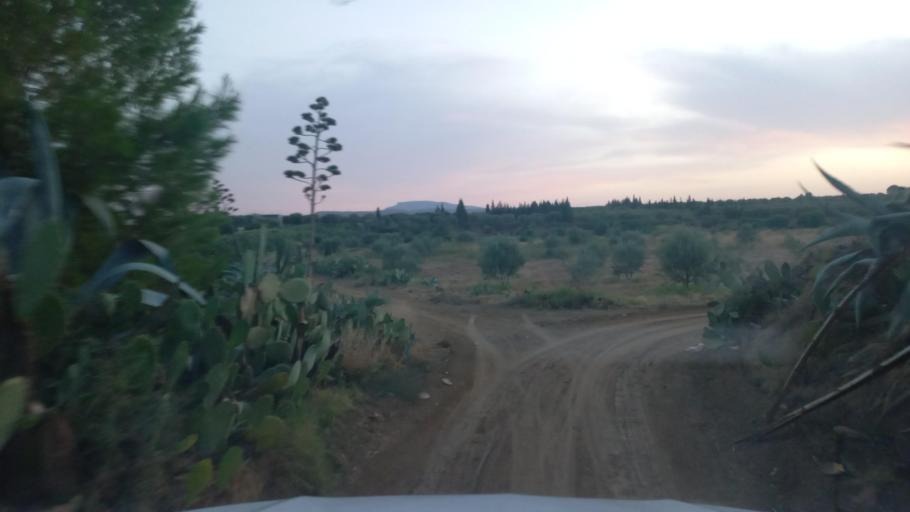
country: TN
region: Al Qasrayn
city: Kasserine
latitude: 35.2318
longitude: 9.0425
